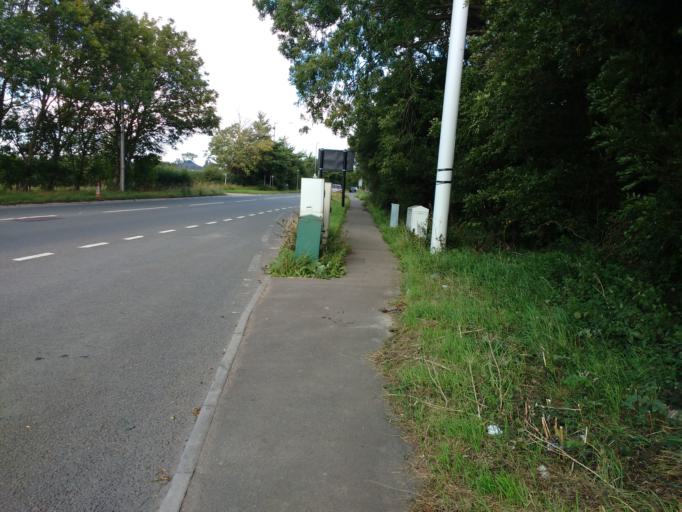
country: GB
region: England
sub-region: North Somerset
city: Dundry
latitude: 51.4200
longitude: -2.6332
